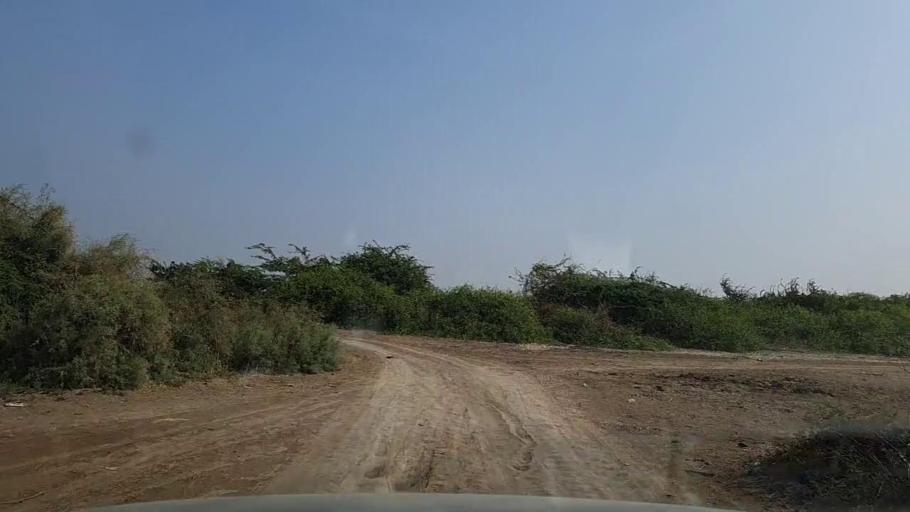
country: PK
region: Sindh
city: Mirpur Sakro
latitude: 24.5523
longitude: 67.5584
